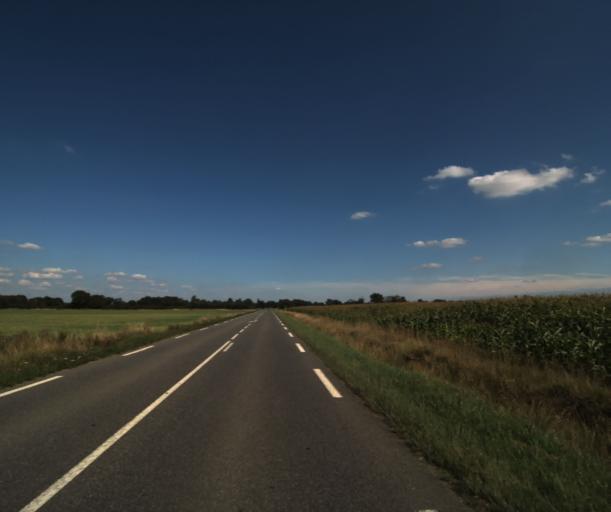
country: FR
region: Midi-Pyrenees
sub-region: Departement de la Haute-Garonne
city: Fonsorbes
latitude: 43.5098
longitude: 1.2285
